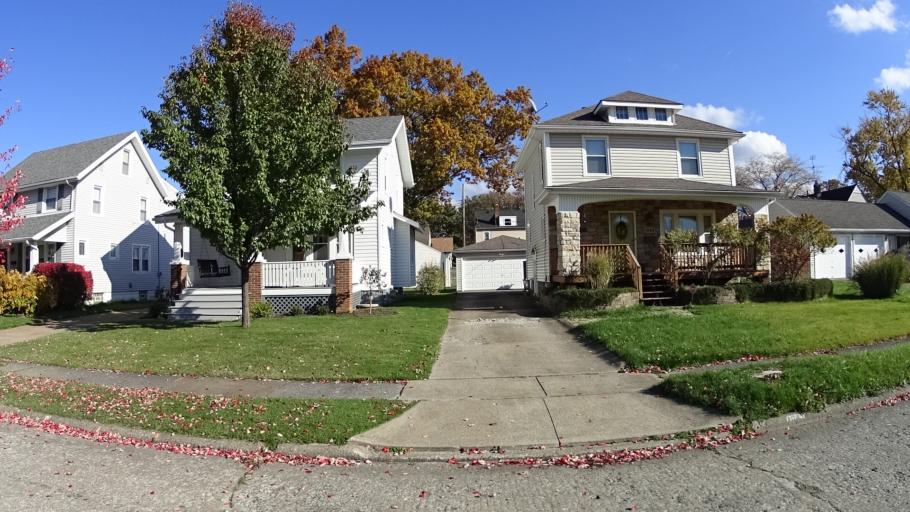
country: US
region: Ohio
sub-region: Lorain County
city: Lorain
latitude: 41.4590
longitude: -82.1909
